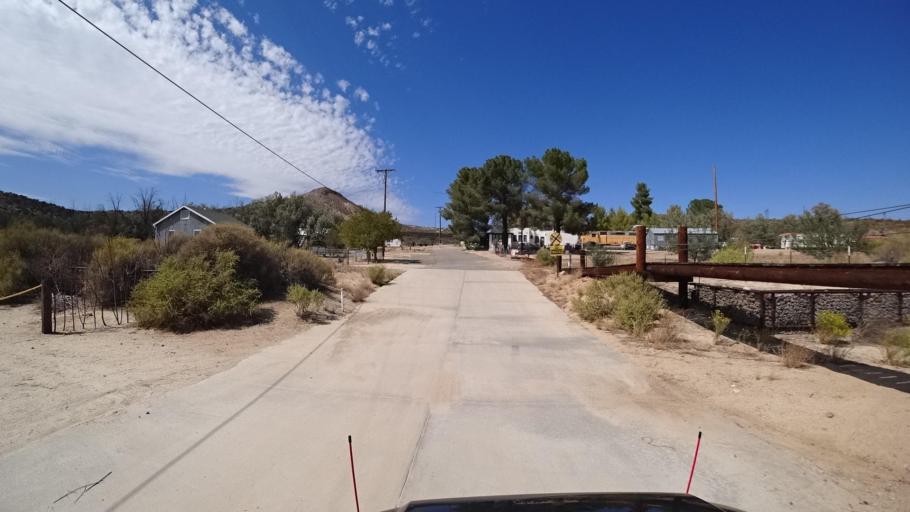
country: MX
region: Baja California
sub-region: Tecate
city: Cereso del Hongo
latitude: 32.6205
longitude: -116.1921
